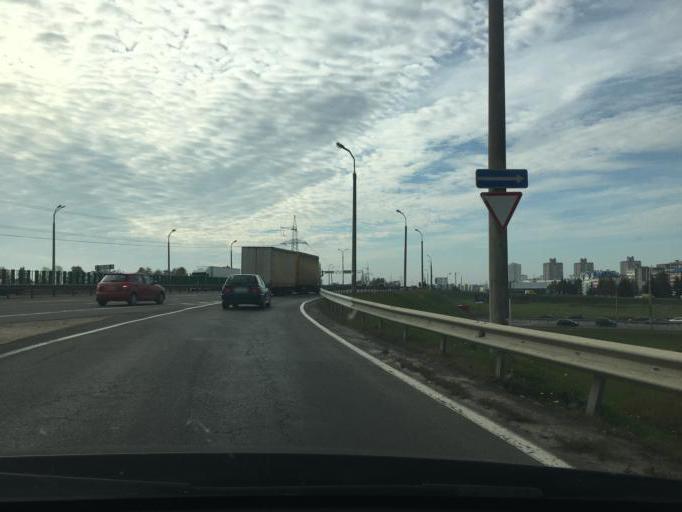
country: BY
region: Minsk
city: Shchomyslitsa
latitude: 53.8425
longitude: 27.4721
